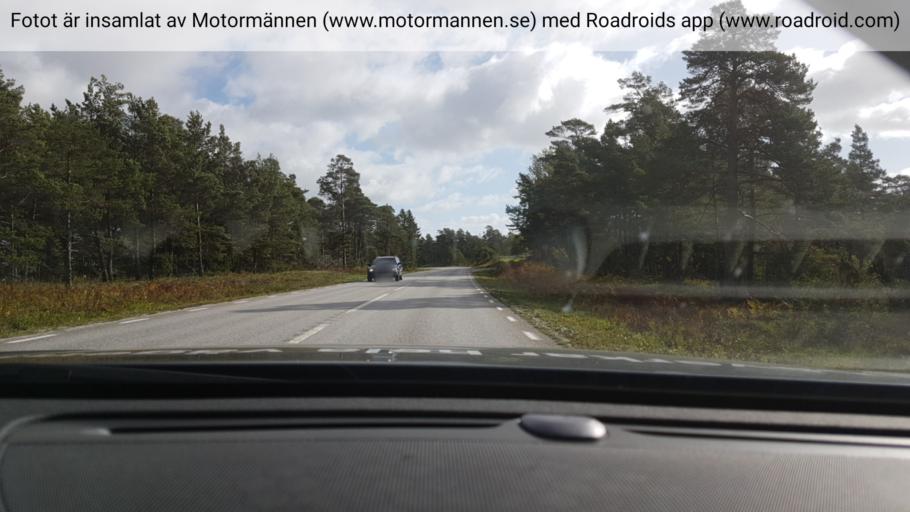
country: SE
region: Gotland
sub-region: Gotland
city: Slite
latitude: 57.8399
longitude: 18.9449
